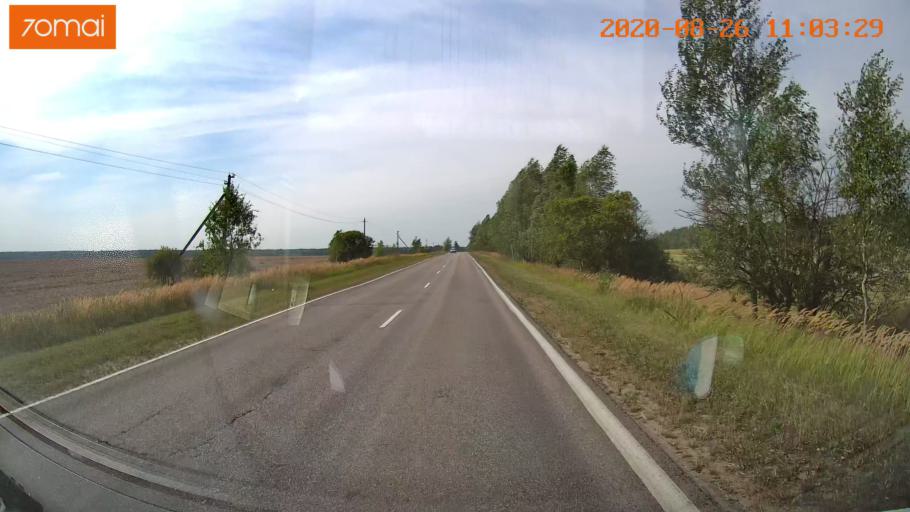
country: RU
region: Rjazan
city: Izhevskoye
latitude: 54.5396
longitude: 41.2102
